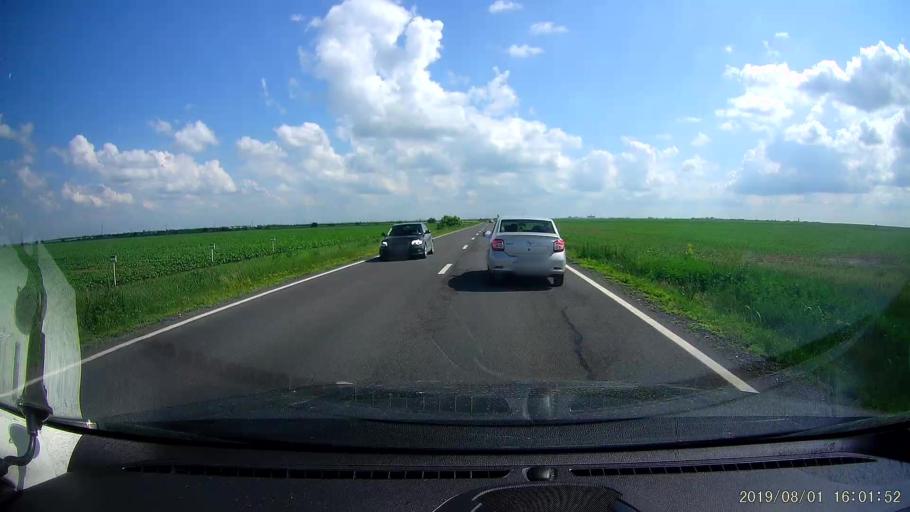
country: RO
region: Ialomita
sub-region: Comuna Ciulnita
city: Ciulnita
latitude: 44.5006
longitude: 27.3891
